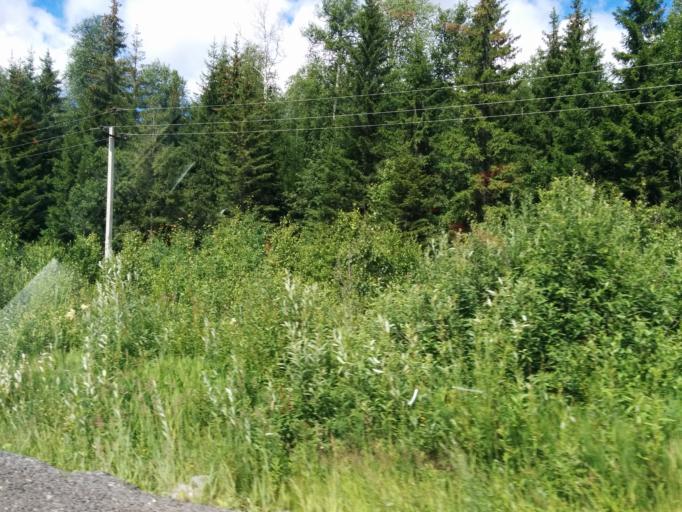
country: RU
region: Perm
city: Kondratovo
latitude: 58.0574
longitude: 56.0788
